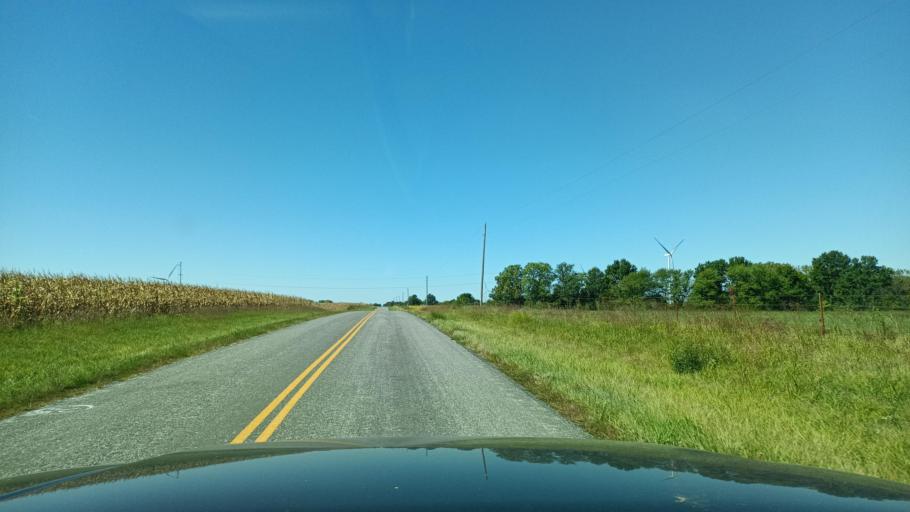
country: US
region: Missouri
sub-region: Adair County
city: Kirksville
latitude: 40.3306
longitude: -92.4865
